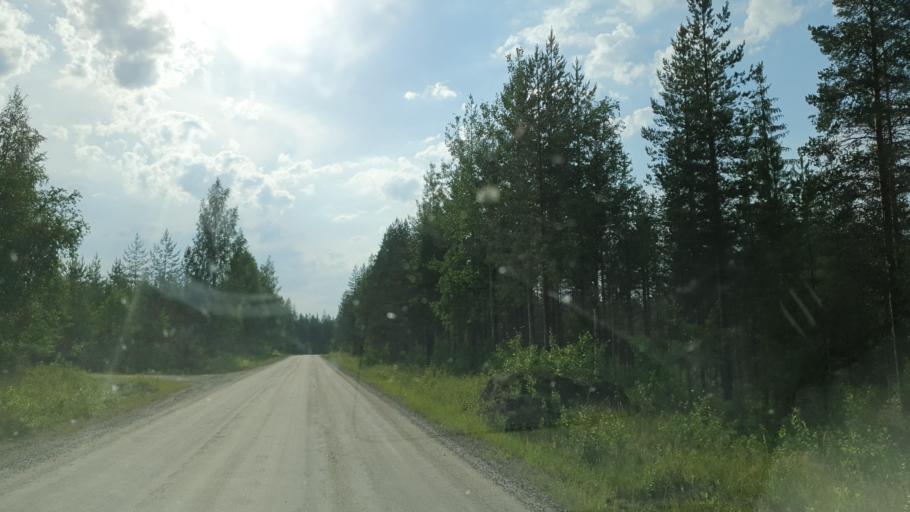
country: FI
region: Kainuu
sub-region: Kehys-Kainuu
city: Kuhmo
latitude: 64.0911
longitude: 29.5887
